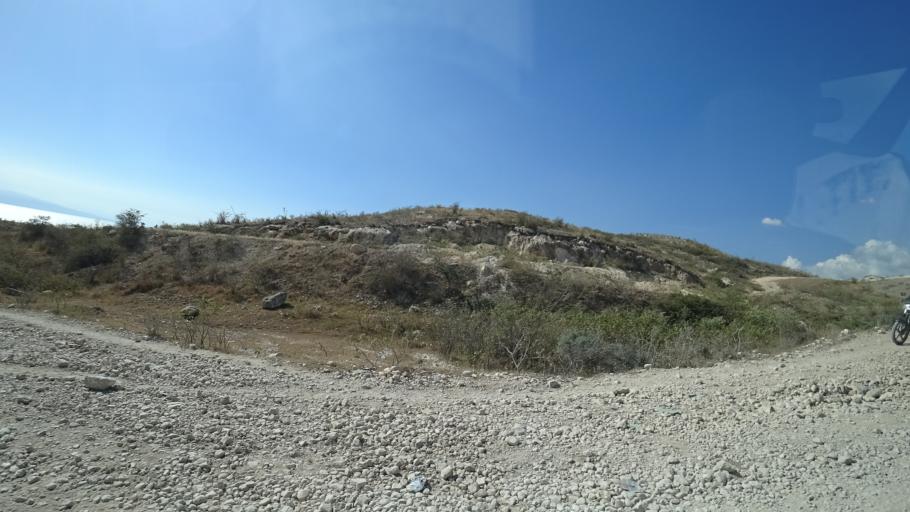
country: HT
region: Ouest
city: Cabaret
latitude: 18.6821
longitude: -72.3187
